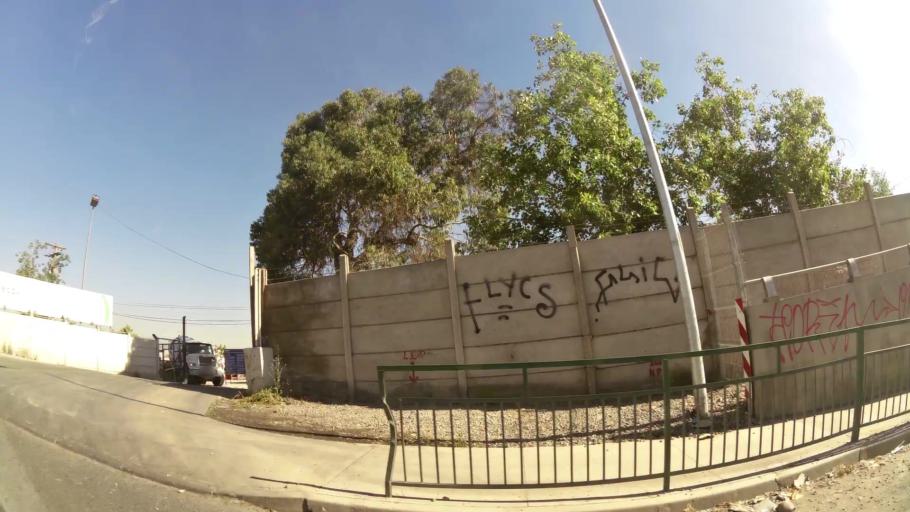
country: CL
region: Santiago Metropolitan
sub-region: Provincia de Maipo
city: San Bernardo
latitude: -33.5558
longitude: -70.6954
